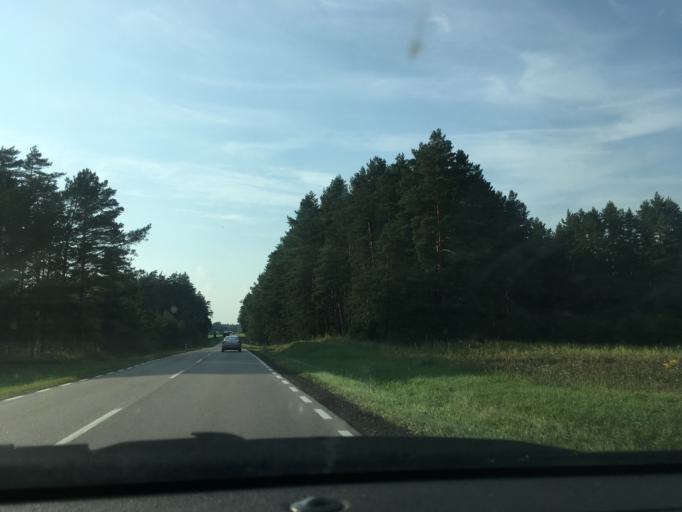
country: PL
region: Podlasie
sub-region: Powiat bialostocki
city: Dobrzyniewo Duze
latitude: 53.2535
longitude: 22.9841
